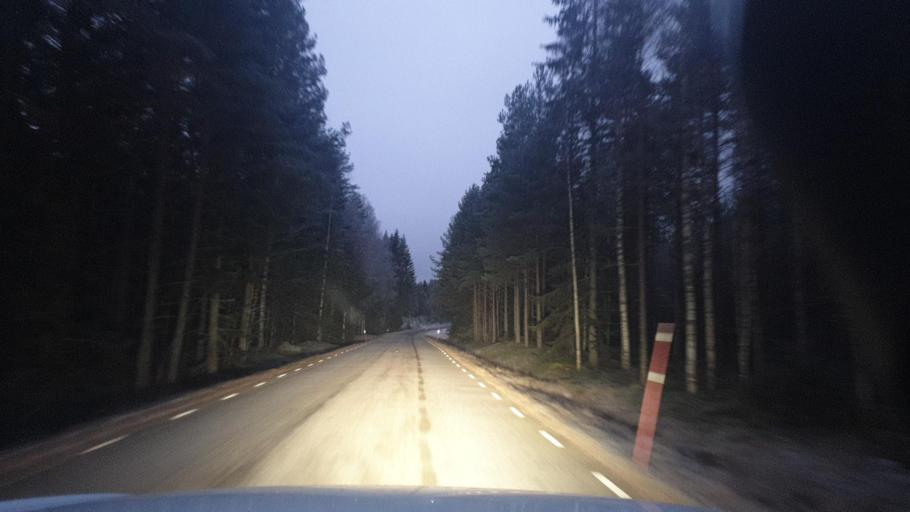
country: SE
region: Vaermland
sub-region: Arvika Kommun
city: Arvika
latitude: 59.5269
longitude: 12.3855
